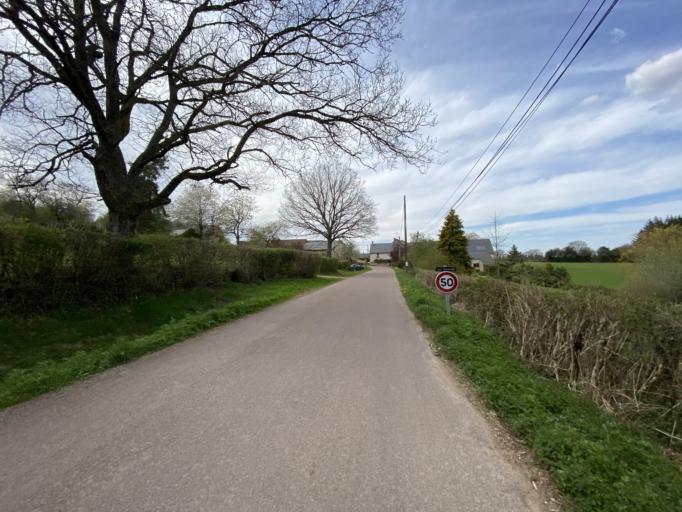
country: FR
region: Bourgogne
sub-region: Departement de la Cote-d'Or
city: Saulieu
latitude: 47.3212
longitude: 4.0815
